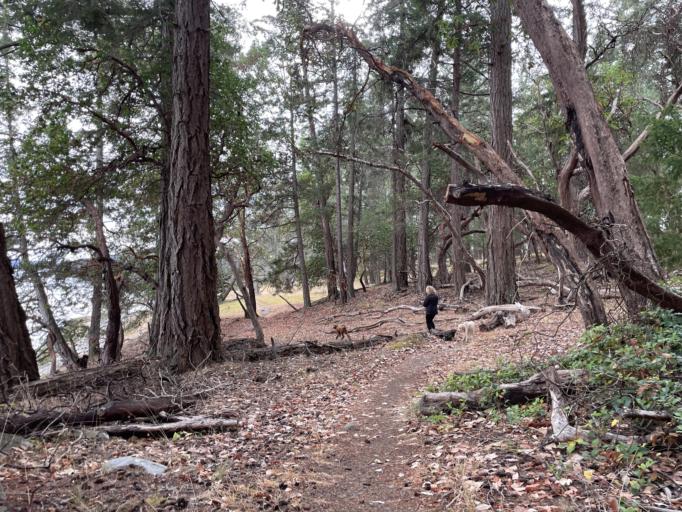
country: CA
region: British Columbia
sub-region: Cowichan Valley Regional District
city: Ladysmith
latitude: 49.0937
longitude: -123.7207
